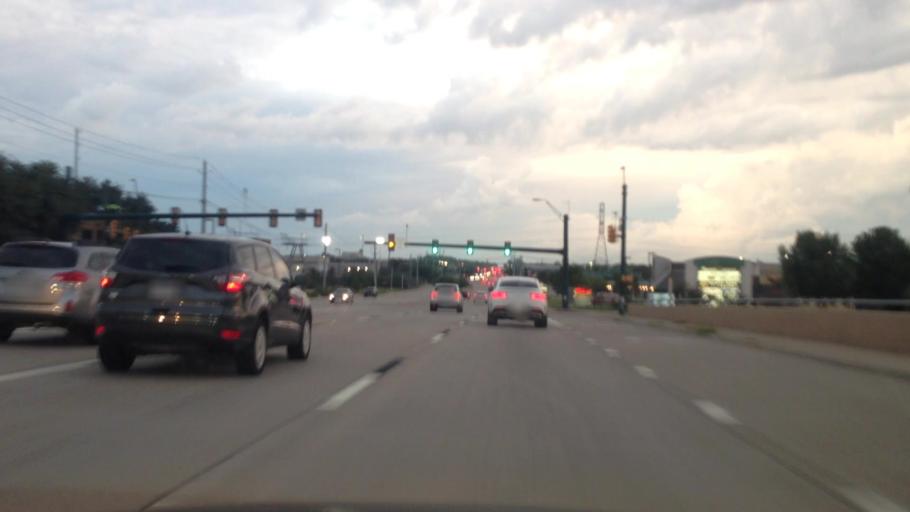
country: US
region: Texas
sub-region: Tarrant County
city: Hurst
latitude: 32.8486
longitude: -97.1861
